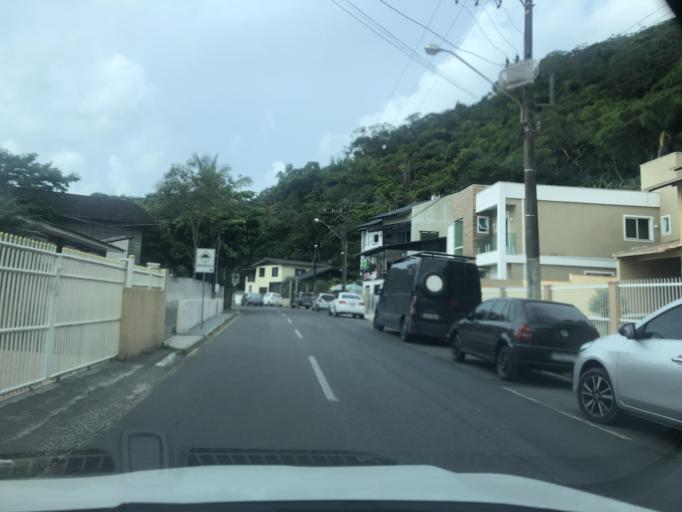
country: BR
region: Santa Catarina
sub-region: Sao Francisco Do Sul
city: Sao Francisco do Sul
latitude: -26.2234
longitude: -48.5007
